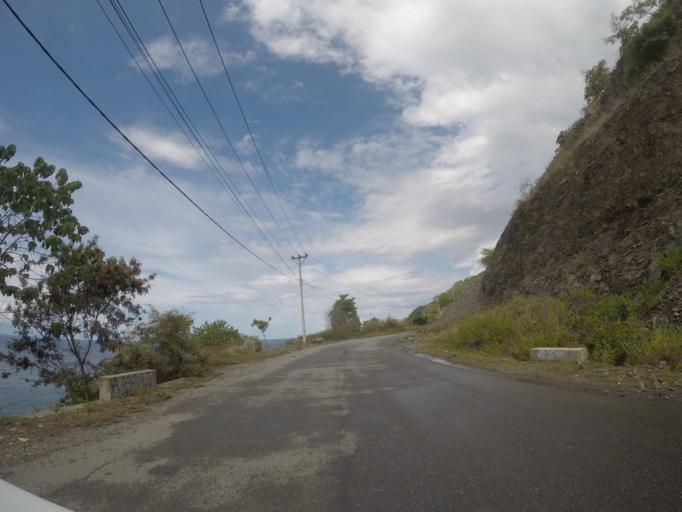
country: TL
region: Liquica
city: Maubara
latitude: -8.6343
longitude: 125.1446
